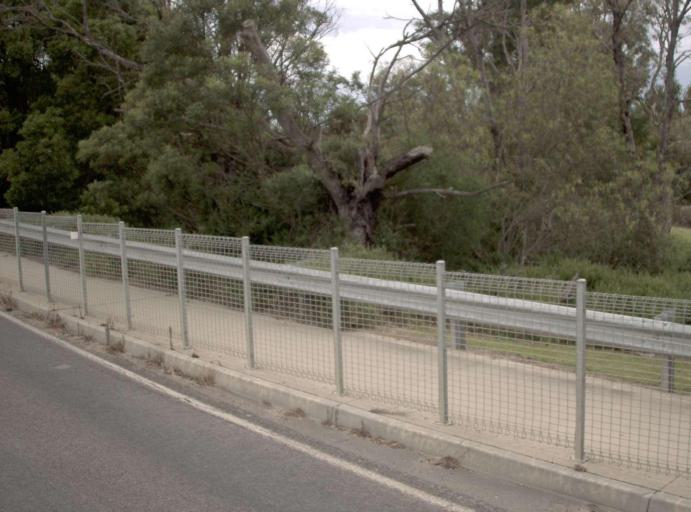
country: AU
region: Victoria
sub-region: East Gippsland
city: Bairnsdale
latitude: -37.8148
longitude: 147.6174
